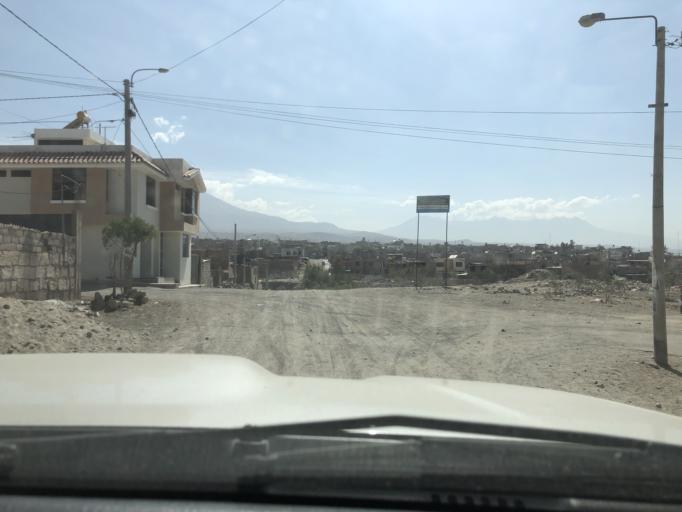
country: PE
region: Arequipa
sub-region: Provincia de Arequipa
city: Arequipa
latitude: -16.3432
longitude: -71.5514
